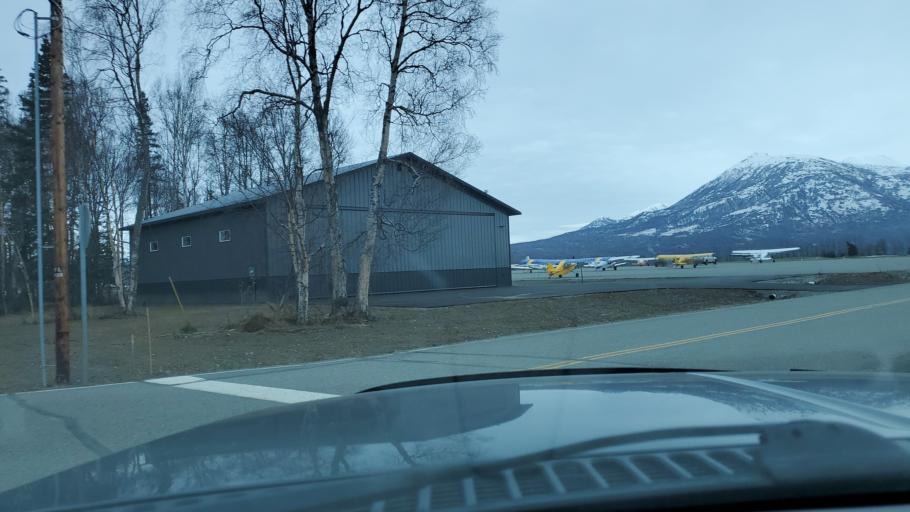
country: US
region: Alaska
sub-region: Matanuska-Susitna Borough
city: Palmer
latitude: 61.5965
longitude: -149.0951
